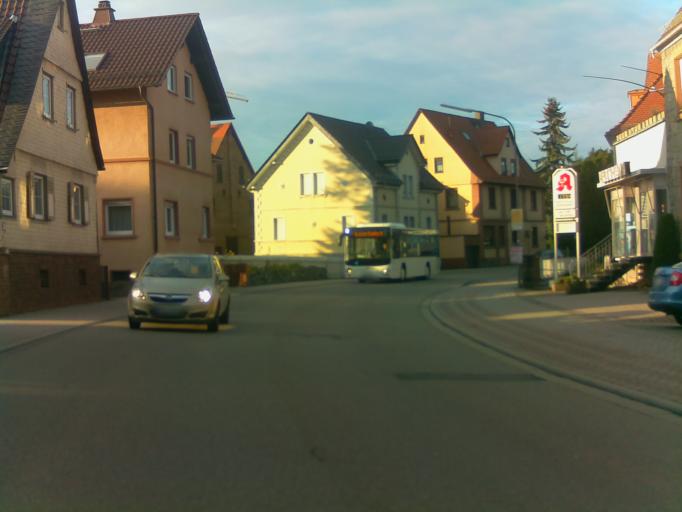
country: DE
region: Hesse
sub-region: Regierungsbezirk Darmstadt
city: Rimbach
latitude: 49.6247
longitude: 8.7559
